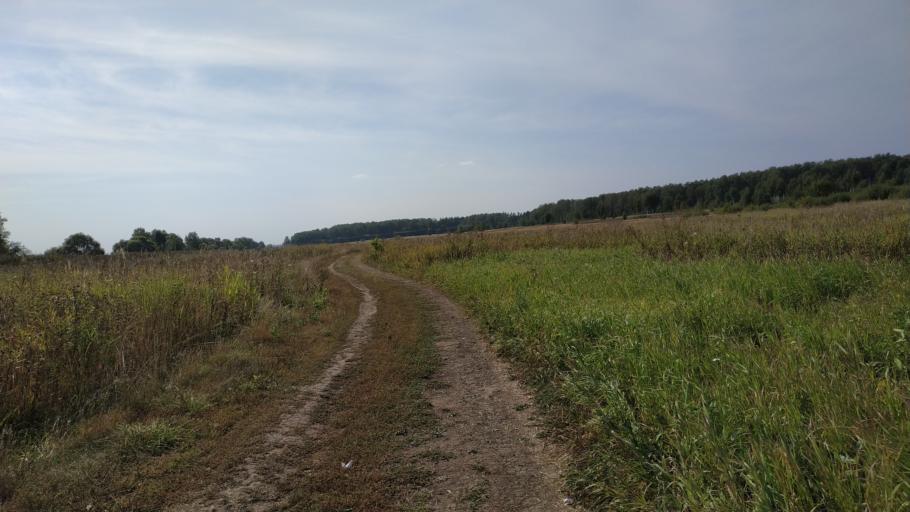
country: RU
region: Moskovskaya
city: Malyshevo
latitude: 55.5319
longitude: 38.3082
